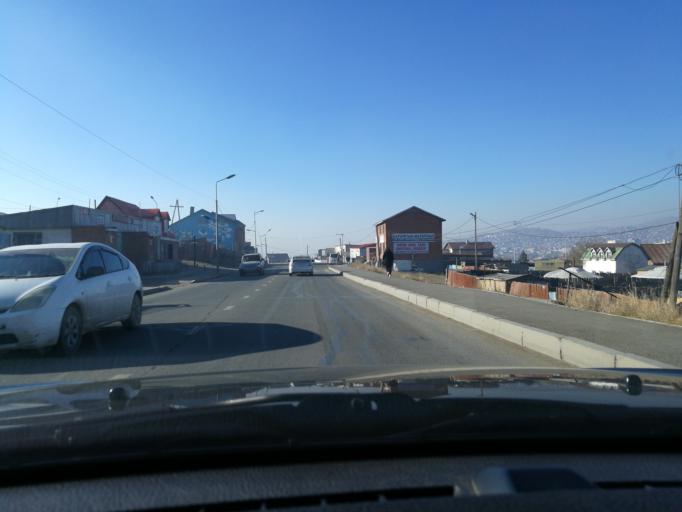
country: MN
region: Ulaanbaatar
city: Ulaanbaatar
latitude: 47.9743
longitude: 106.9322
